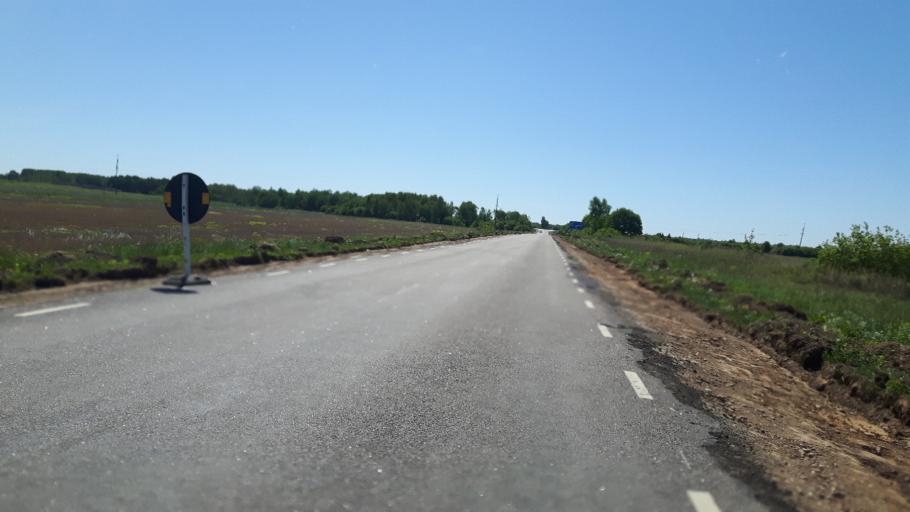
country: EE
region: Ida-Virumaa
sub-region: Narva-Joesuu linn
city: Narva-Joesuu
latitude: 59.3841
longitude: 27.9208
